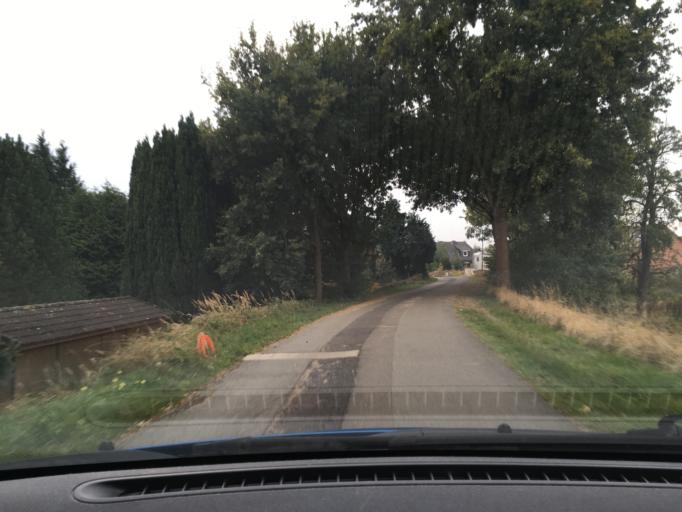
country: DE
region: Lower Saxony
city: Drage
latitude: 53.4130
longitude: 10.2615
